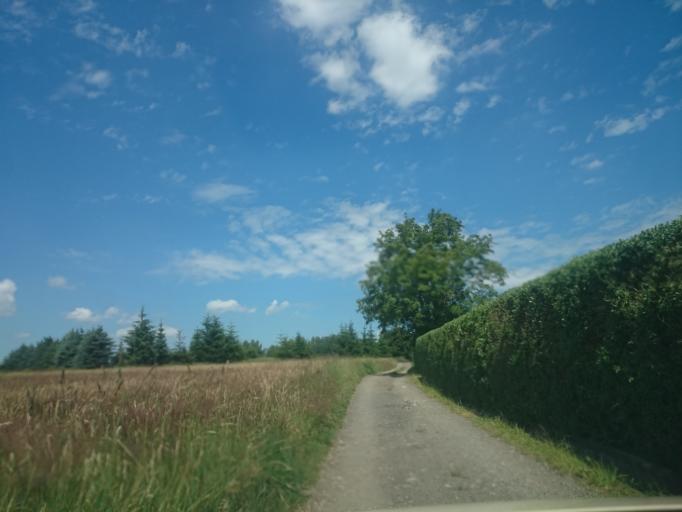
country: DE
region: Saxony
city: Freiberg
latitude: 50.9240
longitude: 13.3543
